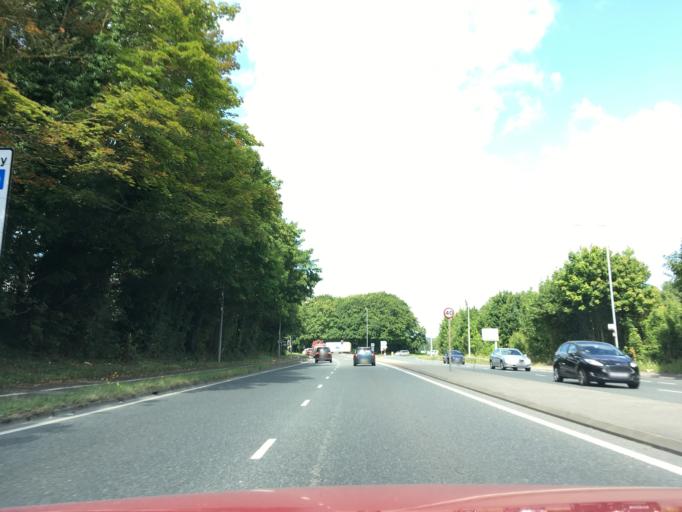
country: GB
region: England
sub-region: Kent
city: Aylesford
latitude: 51.2914
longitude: 0.4859
